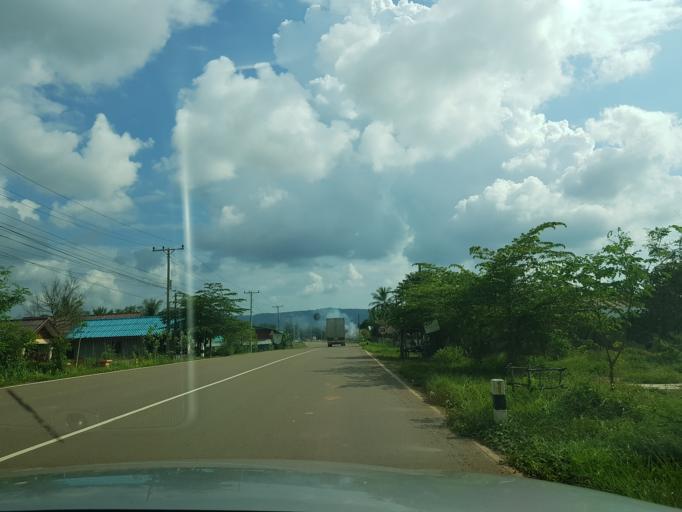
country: TH
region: Nong Khai
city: Sangkhom
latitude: 18.0836
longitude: 102.2931
